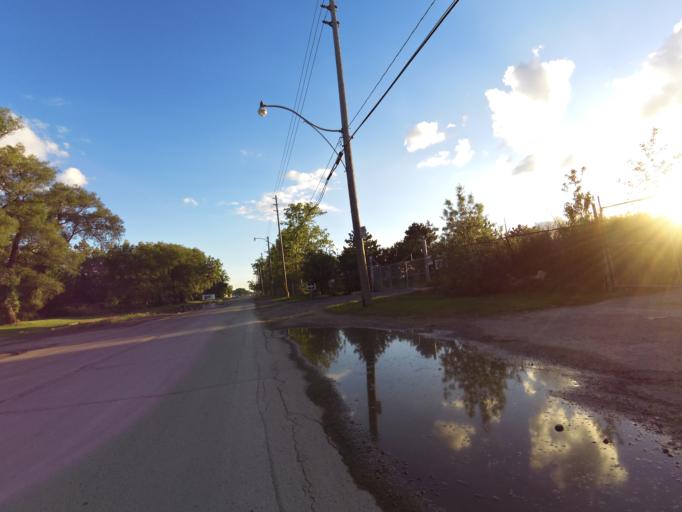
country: CA
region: Ontario
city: Toronto
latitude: 43.6405
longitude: -79.3442
